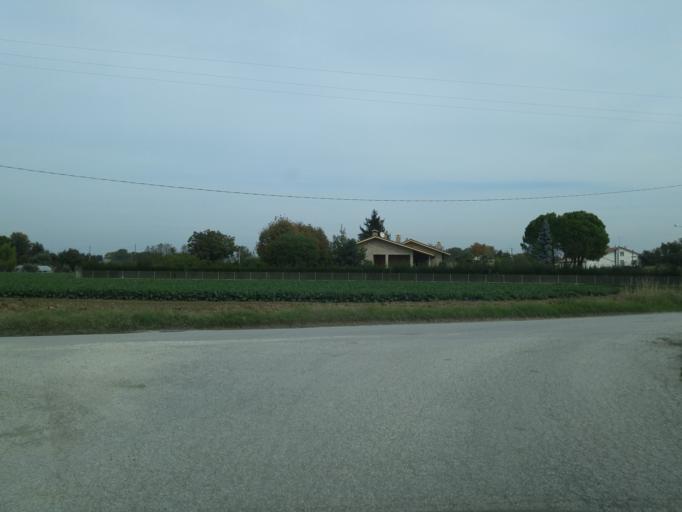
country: IT
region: The Marches
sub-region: Provincia di Pesaro e Urbino
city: Cuccurano
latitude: 43.7822
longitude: 12.9750
